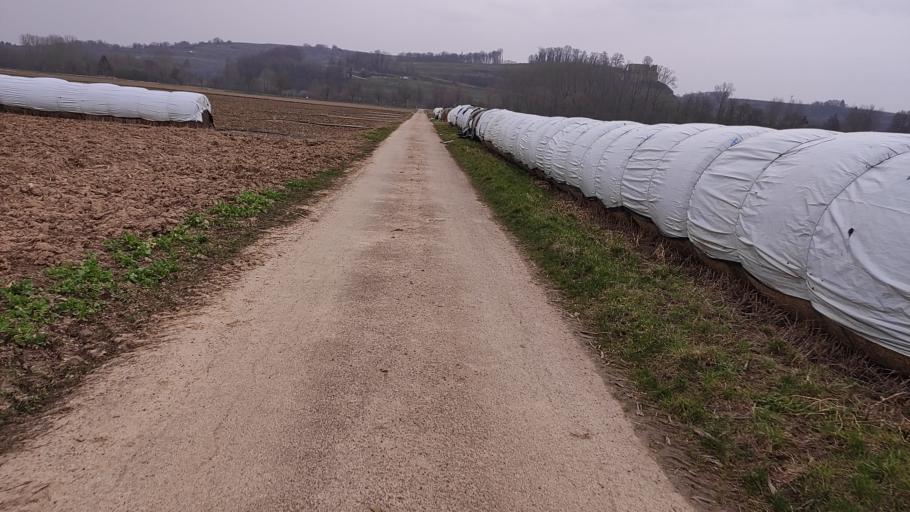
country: DE
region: Baden-Wuerttemberg
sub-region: Freiburg Region
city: Riegel
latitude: 48.1731
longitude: 7.7562
